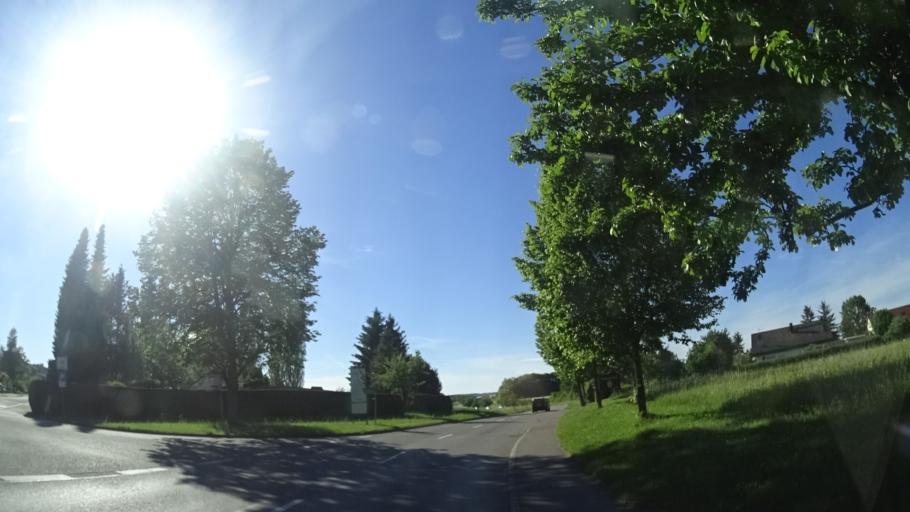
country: DE
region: Baden-Wuerttemberg
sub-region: Regierungsbezirk Stuttgart
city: Buhlertann
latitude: 49.0417
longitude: 9.9022
